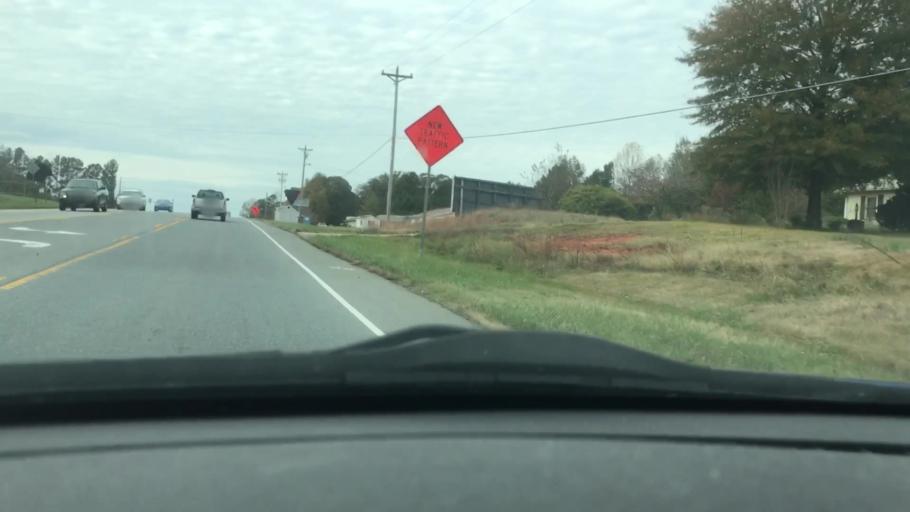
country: US
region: North Carolina
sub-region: Randolph County
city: Asheboro
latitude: 35.6919
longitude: -79.8514
